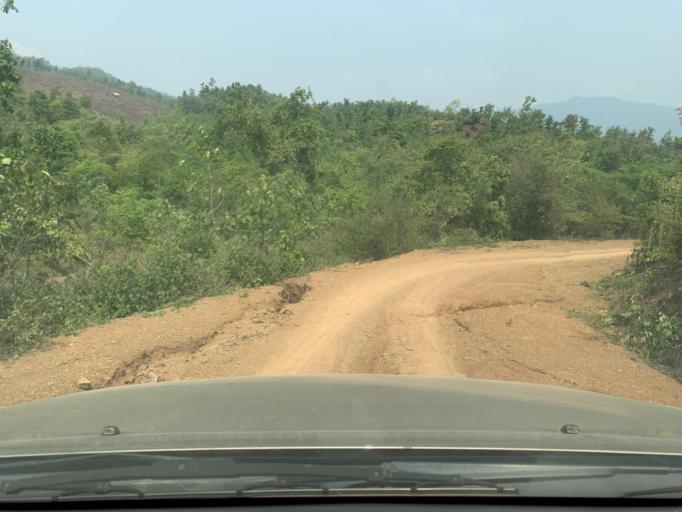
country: LA
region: Louangphabang
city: Louangphabang
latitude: 19.9376
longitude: 102.1323
